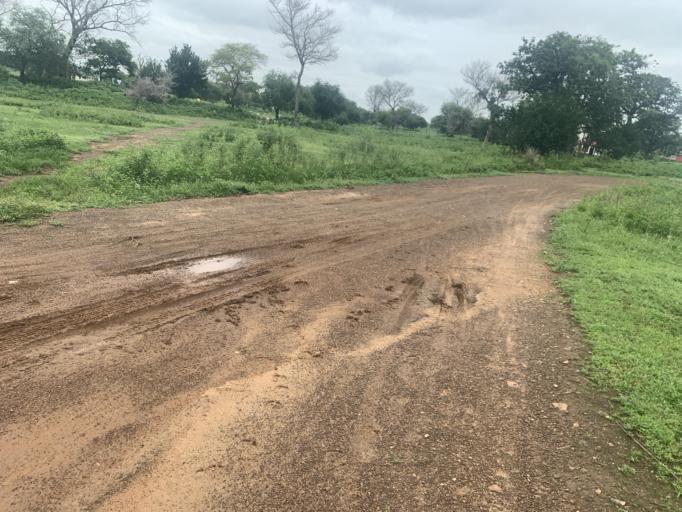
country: GH
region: Upper East
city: Navrongo
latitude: 10.8658
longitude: -1.0813
